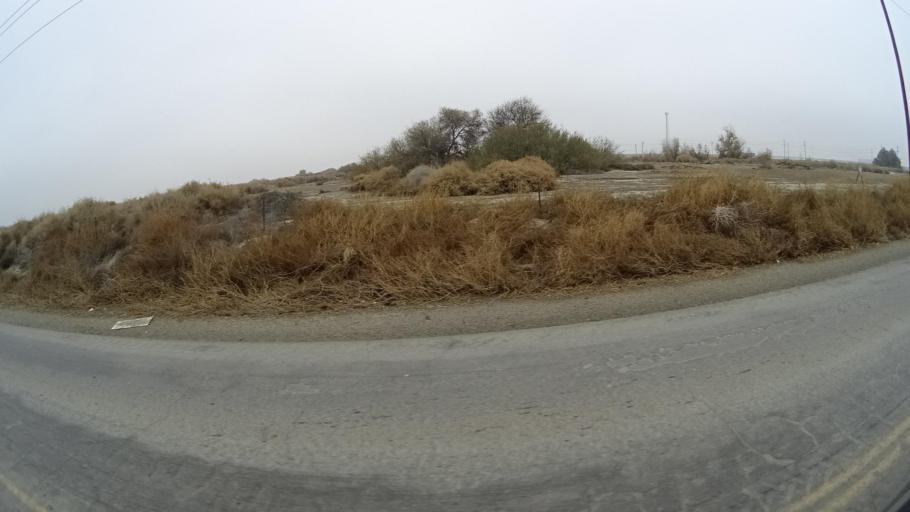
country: US
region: California
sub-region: Kern County
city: Greenfield
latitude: 35.2091
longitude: -119.1680
